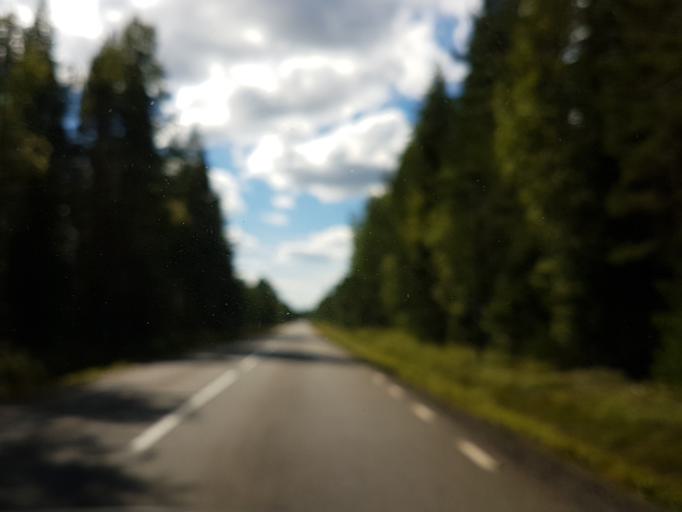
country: SE
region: Vaesterbotten
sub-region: Umea Kommun
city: Saevar
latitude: 64.1384
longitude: 20.5834
